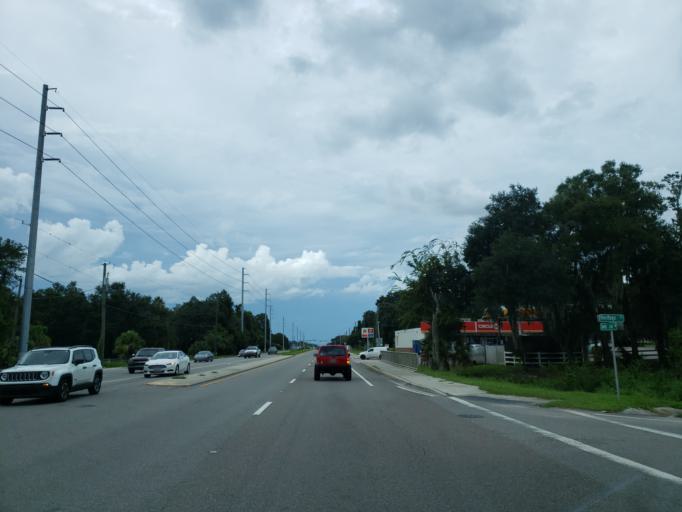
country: US
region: Florida
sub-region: Polk County
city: Willow Oak
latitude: 27.9486
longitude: -82.0553
